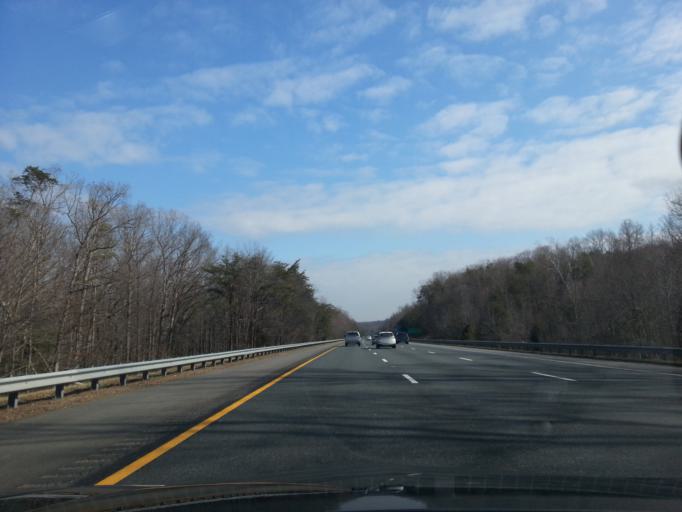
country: US
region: Virginia
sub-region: Stafford County
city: Stafford
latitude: 38.4338
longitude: -77.4145
